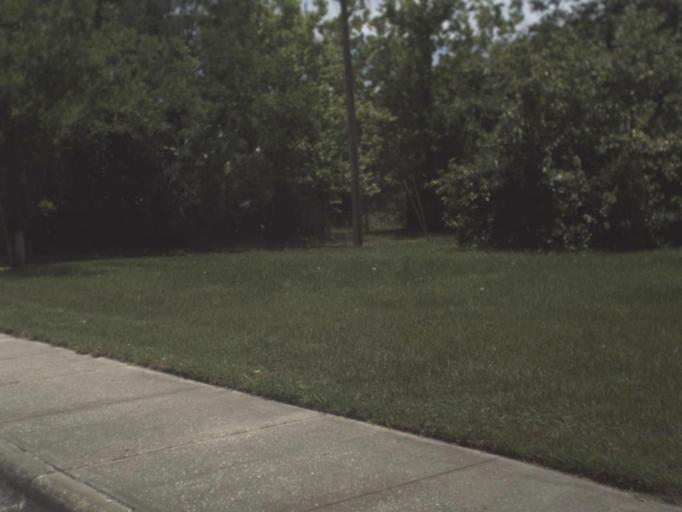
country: US
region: Florida
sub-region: Duval County
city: Jacksonville
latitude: 30.3525
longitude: -81.7058
